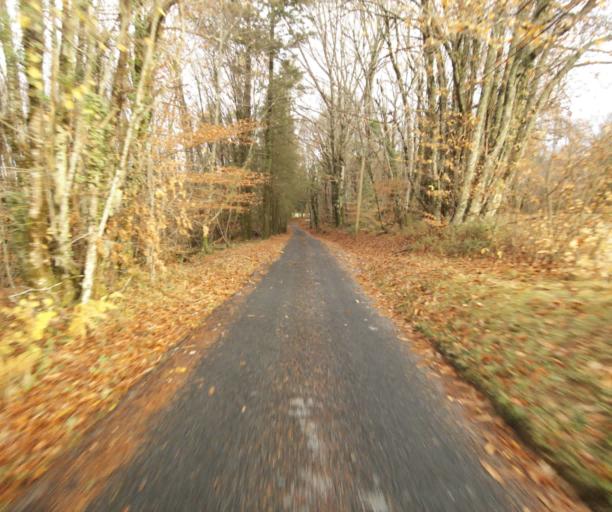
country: FR
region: Limousin
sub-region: Departement de la Correze
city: Cornil
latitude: 45.2051
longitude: 1.7127
